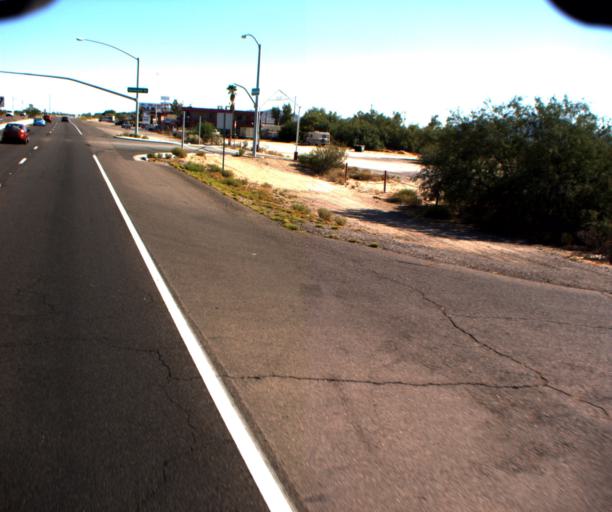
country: US
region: Arizona
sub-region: Pinal County
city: Casa Grande
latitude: 32.9706
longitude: -111.7566
